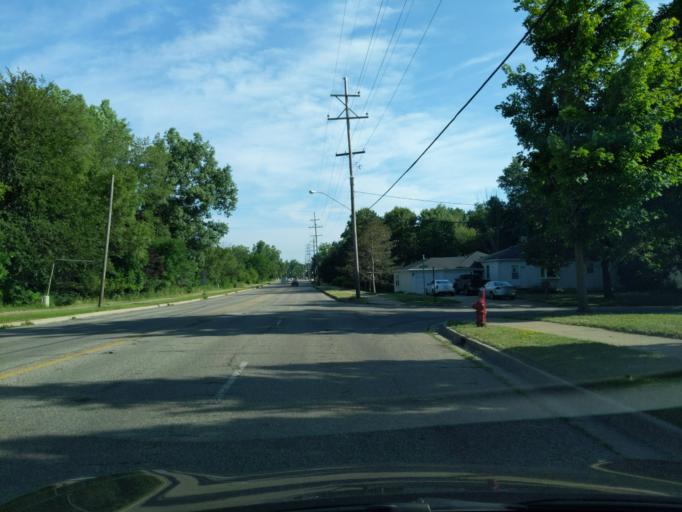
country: US
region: Michigan
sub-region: Ingham County
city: Okemos
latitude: 42.7260
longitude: -84.4276
